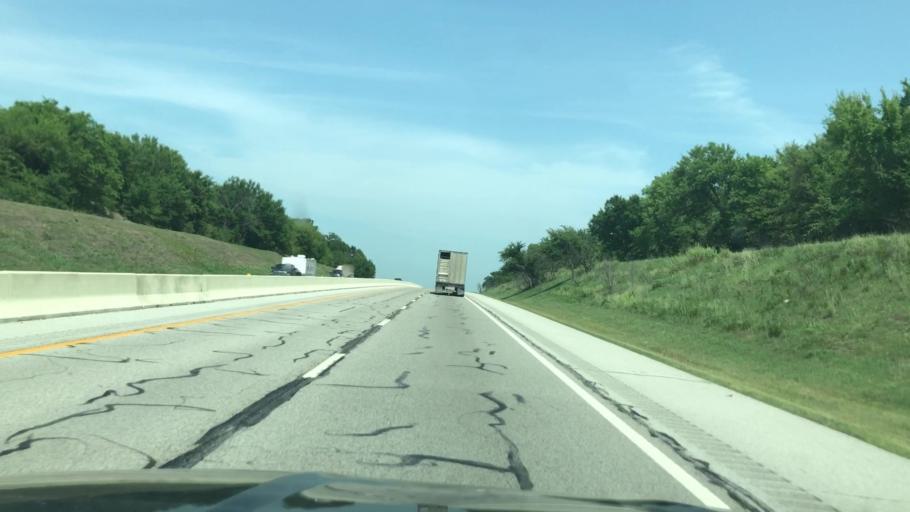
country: US
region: Oklahoma
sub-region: Rogers County
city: Chelsea
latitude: 36.4661
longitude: -95.3402
